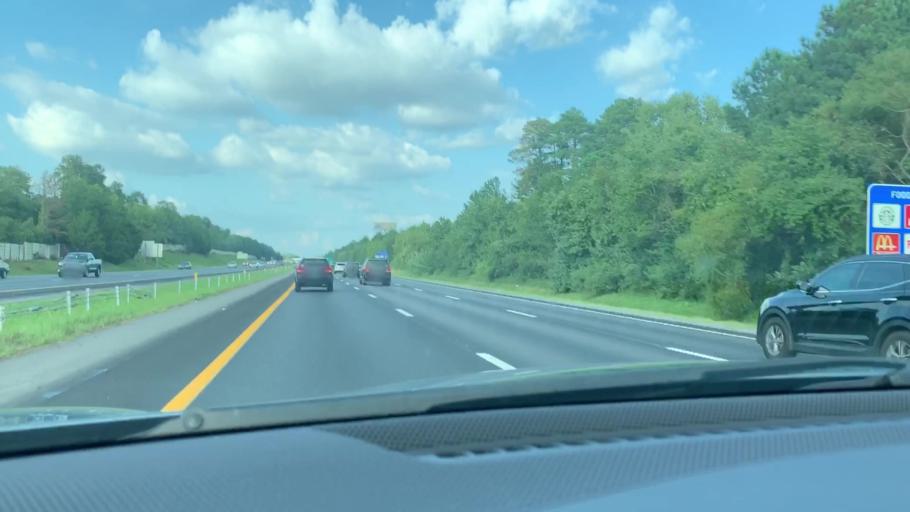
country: US
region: South Carolina
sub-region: Richland County
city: Forest Acres
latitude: 34.0071
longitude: -80.9553
